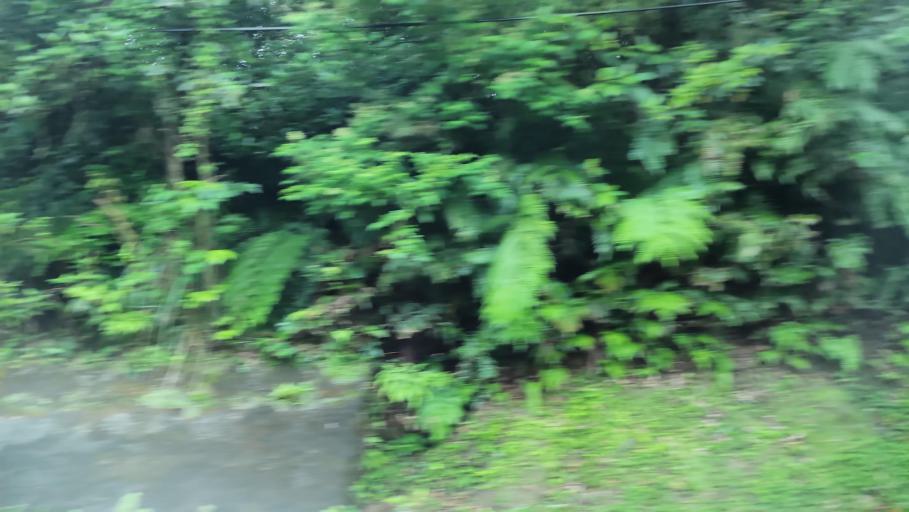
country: TW
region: Taipei
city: Taipei
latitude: 25.1436
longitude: 121.6094
